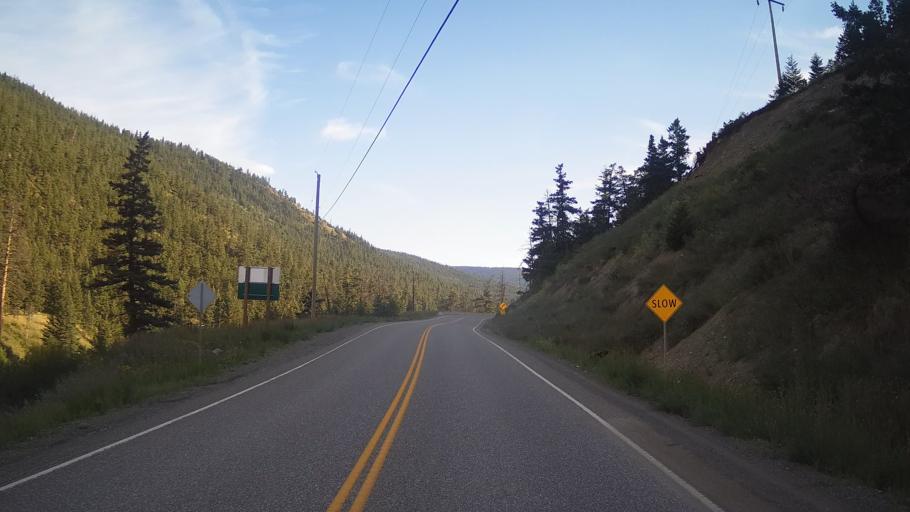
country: CA
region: British Columbia
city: Cache Creek
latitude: 50.8652
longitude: -121.5265
